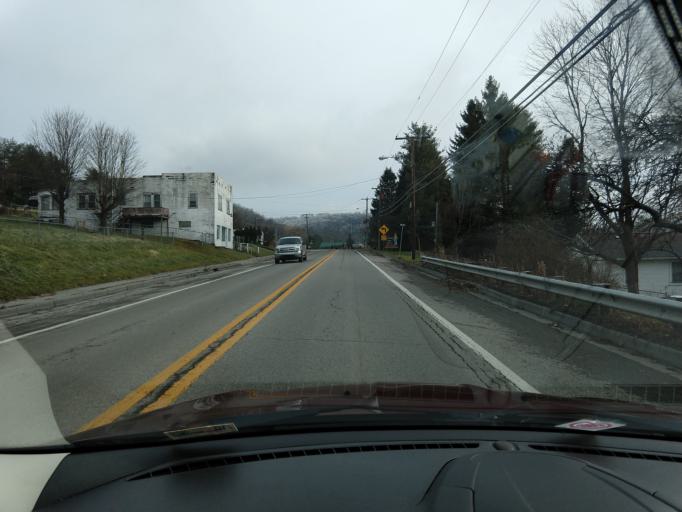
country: US
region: West Virginia
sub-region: Greenbrier County
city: Rainelle
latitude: 38.0564
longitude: -80.7083
